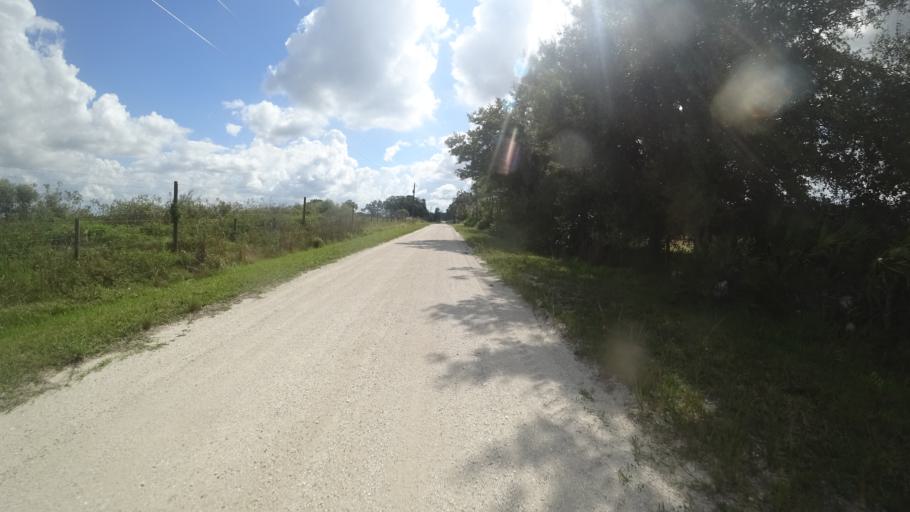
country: US
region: Florida
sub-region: Hillsborough County
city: Wimauma
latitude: 27.5489
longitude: -82.1745
